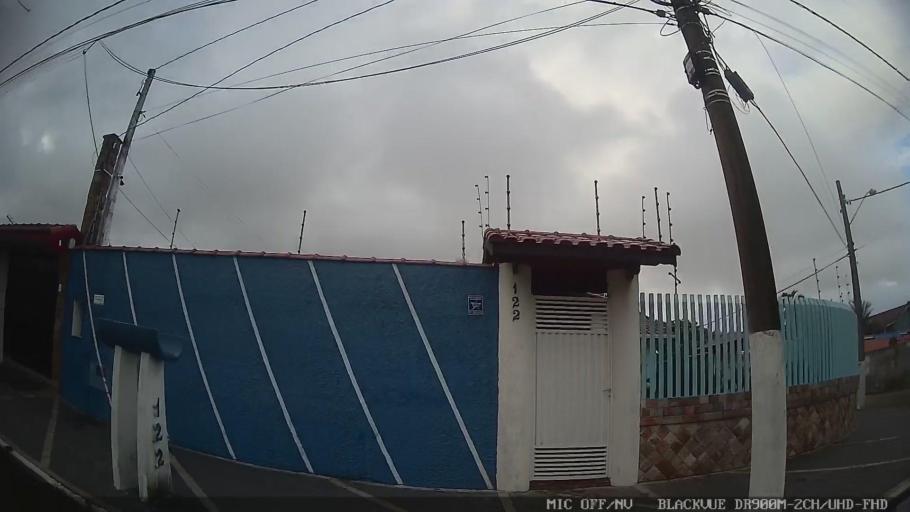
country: BR
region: Sao Paulo
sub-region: Itanhaem
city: Itanhaem
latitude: -24.2168
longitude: -46.8473
